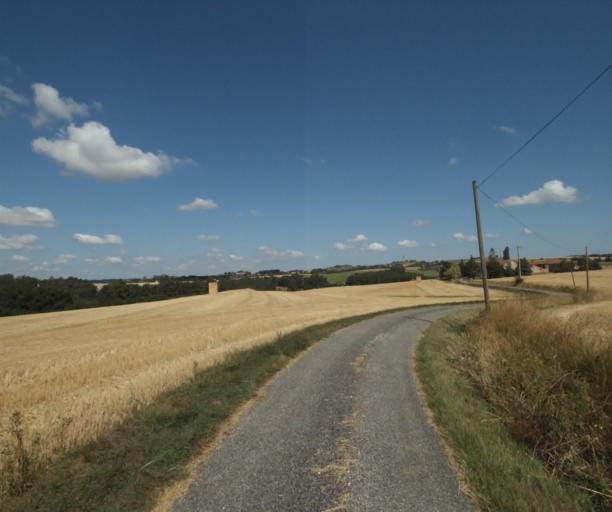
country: FR
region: Midi-Pyrenees
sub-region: Departement de la Haute-Garonne
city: Auriac-sur-Vendinelle
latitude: 43.4524
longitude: 1.7840
